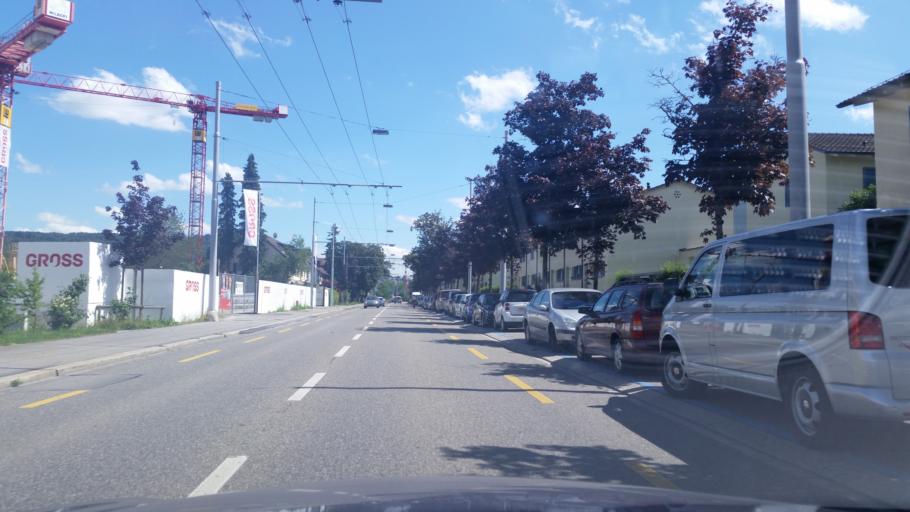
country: CH
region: Zurich
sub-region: Bezirk Zuerich
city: Zuerich (Kreis 11) / Oerlikon
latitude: 47.4063
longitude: 8.5319
